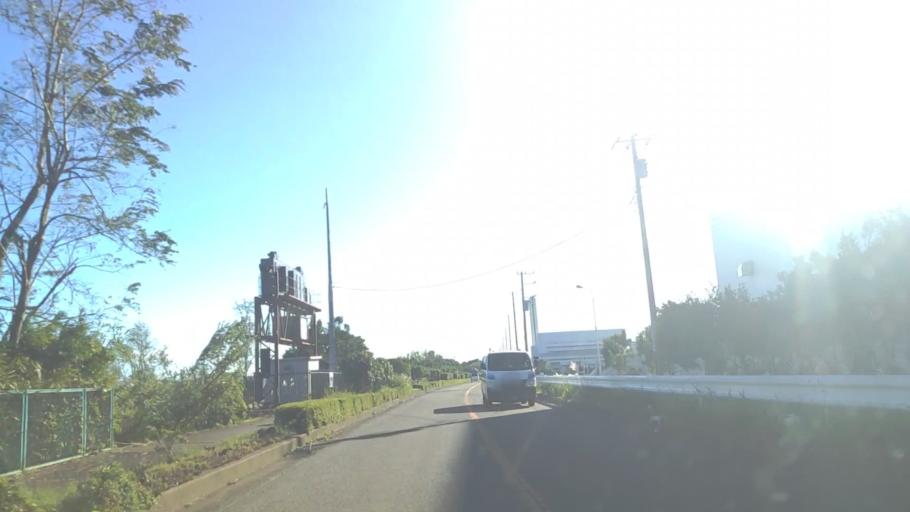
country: JP
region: Kanagawa
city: Atsugi
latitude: 35.4618
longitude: 139.3769
